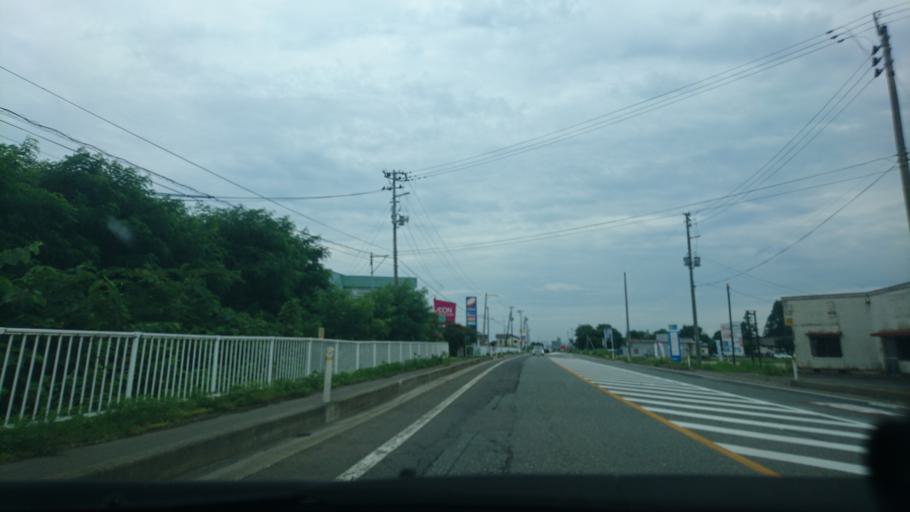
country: JP
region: Akita
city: Omagari
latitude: 39.4172
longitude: 140.5423
